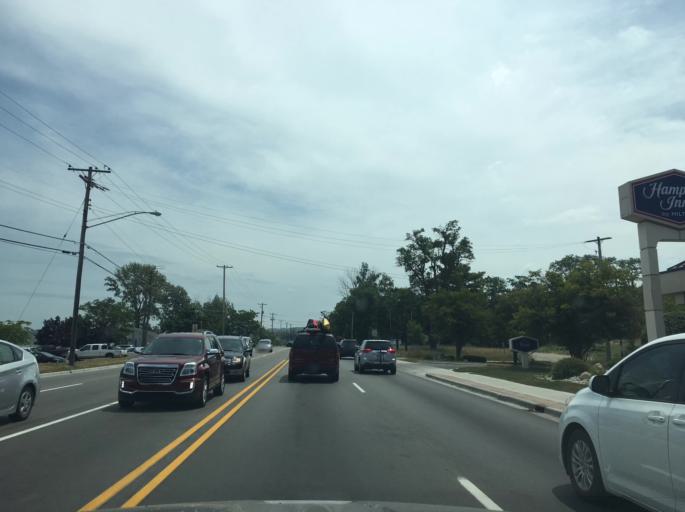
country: US
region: Michigan
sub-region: Grand Traverse County
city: Traverse City
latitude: 44.7486
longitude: -85.5564
